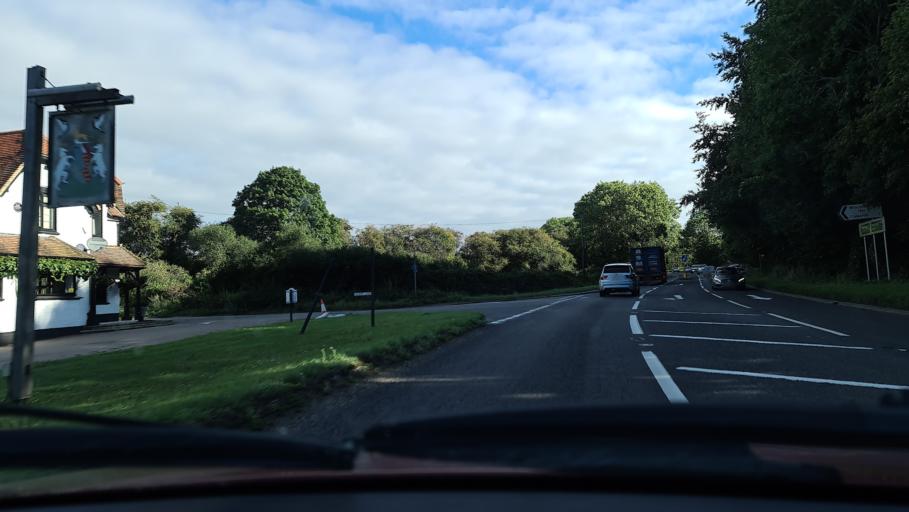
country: GB
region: England
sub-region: Buckinghamshire
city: Seer Green
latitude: 51.6372
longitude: -0.6200
